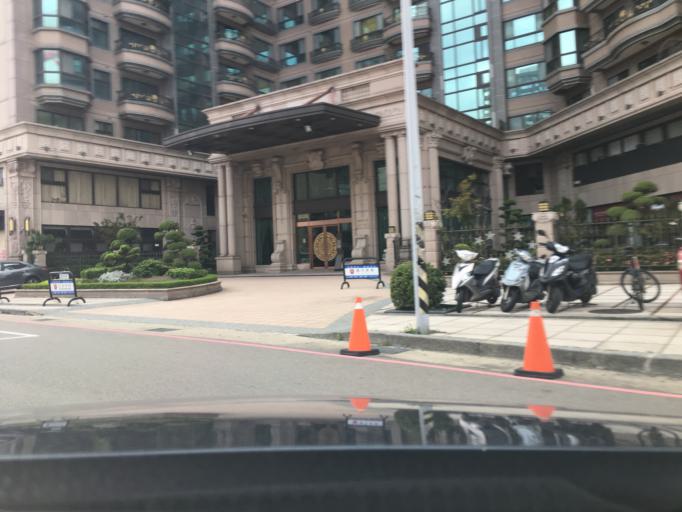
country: TW
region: Taiwan
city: Taoyuan City
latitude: 25.0532
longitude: 121.2873
